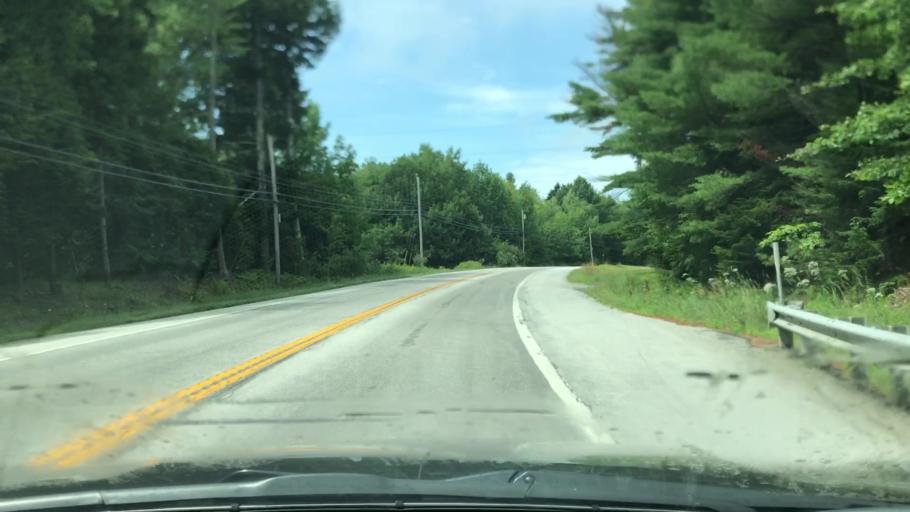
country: US
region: Maine
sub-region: Waldo County
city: Northport
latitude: 44.3428
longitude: -68.9689
